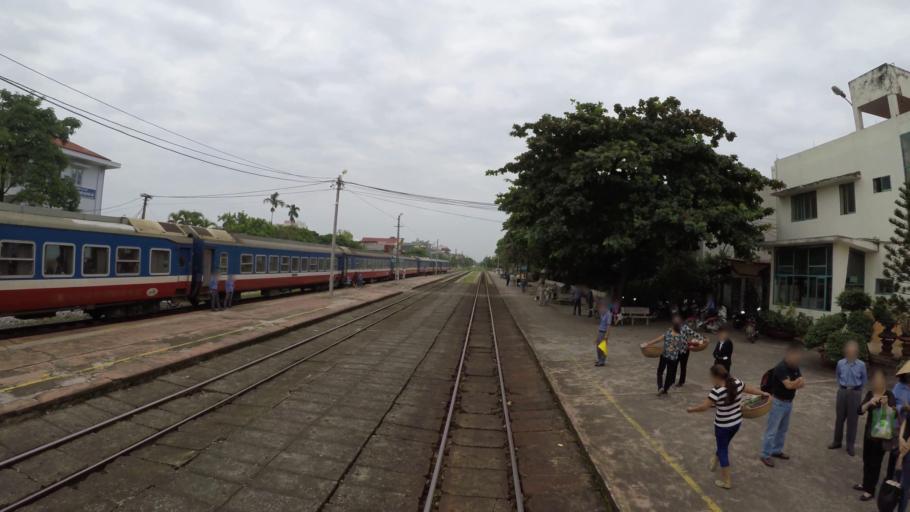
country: VN
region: Hai Duong
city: Thanh Pho Hai Duong
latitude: 20.9427
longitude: 106.3002
